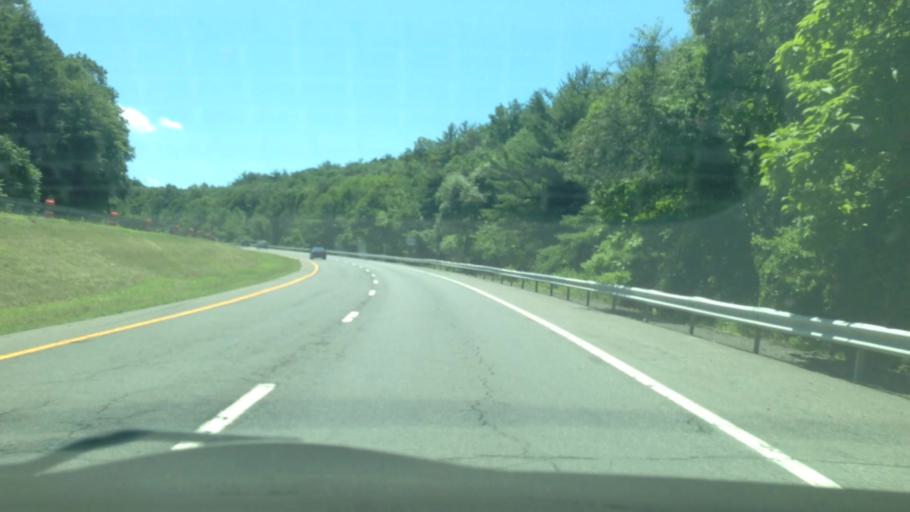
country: US
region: New York
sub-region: Ulster County
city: Lake Katrine
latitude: 41.9733
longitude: -74.0200
